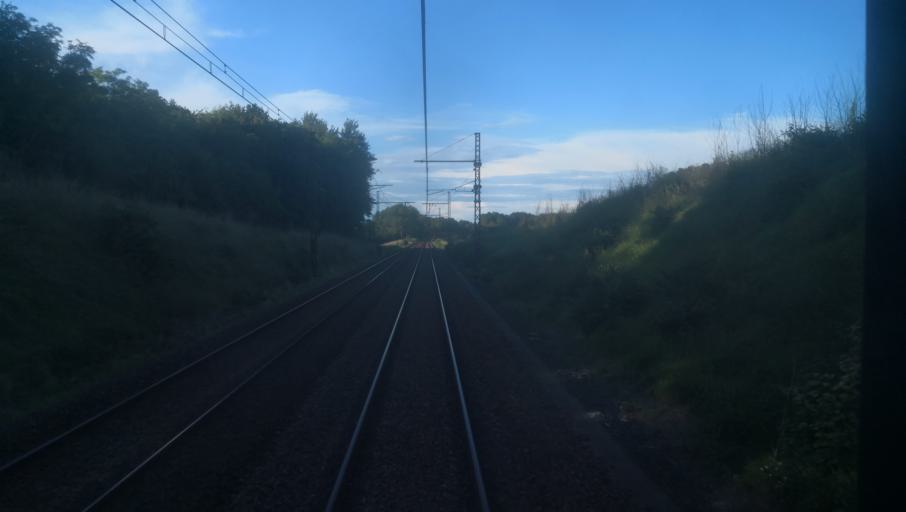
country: FR
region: Centre
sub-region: Departement du Cher
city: Mereau
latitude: 47.1768
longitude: 2.0621
